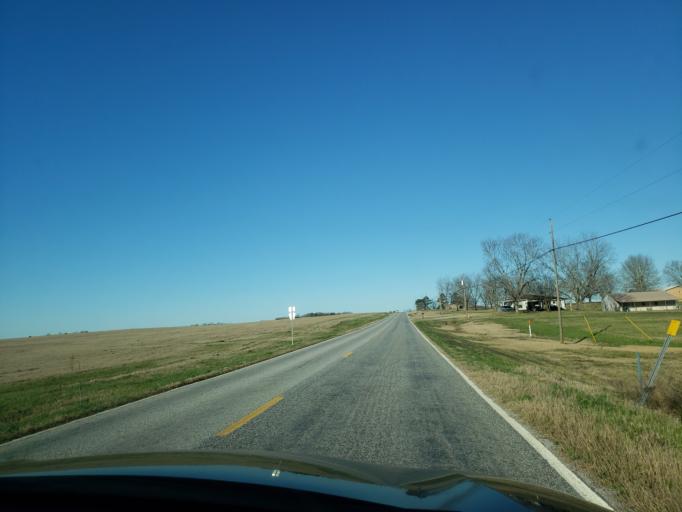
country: US
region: Alabama
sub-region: Elmore County
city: Tallassee
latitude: 32.5813
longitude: -85.7753
